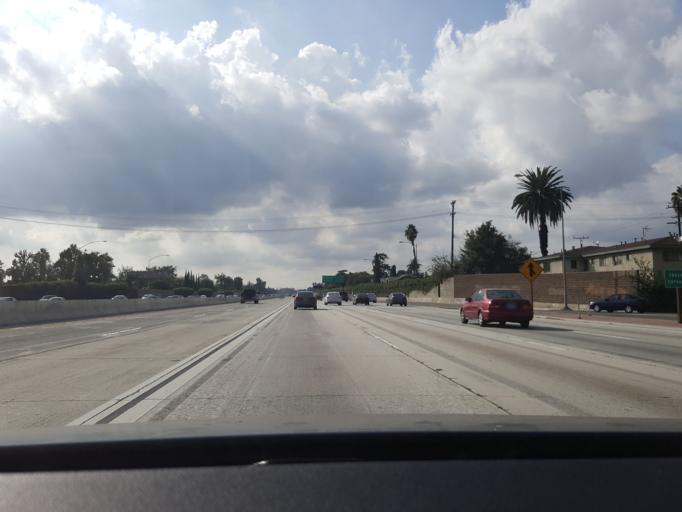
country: US
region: California
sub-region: Los Angeles County
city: Monterey Park
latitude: 34.0718
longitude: -118.1232
